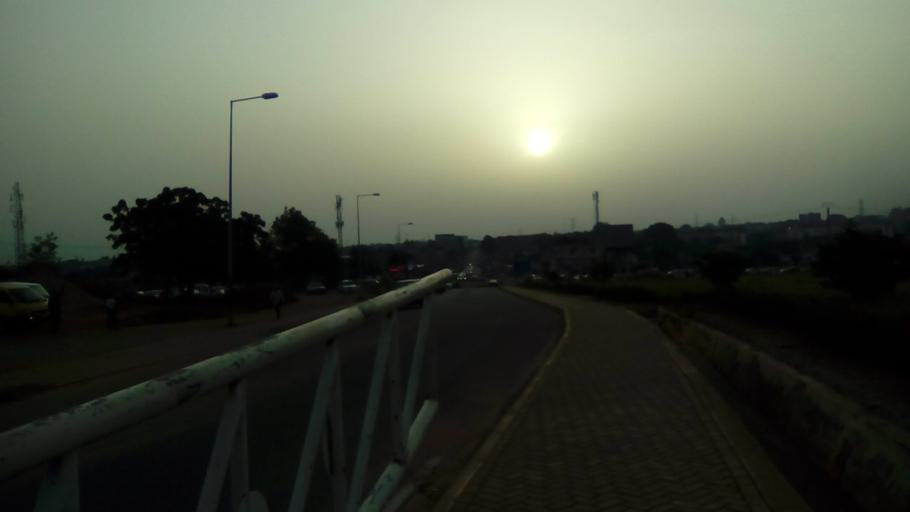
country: GH
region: Greater Accra
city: Medina Estates
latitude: 5.6405
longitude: -0.1798
